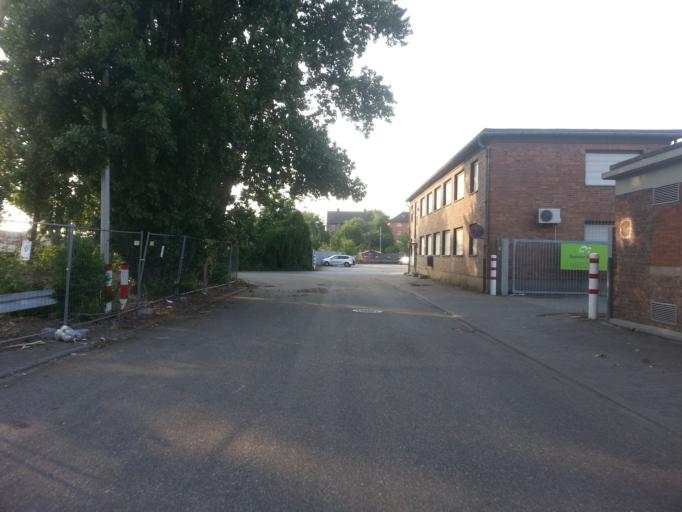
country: DE
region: Rheinland-Pfalz
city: Ludwigshafen am Rhein
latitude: 49.5008
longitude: 8.4475
